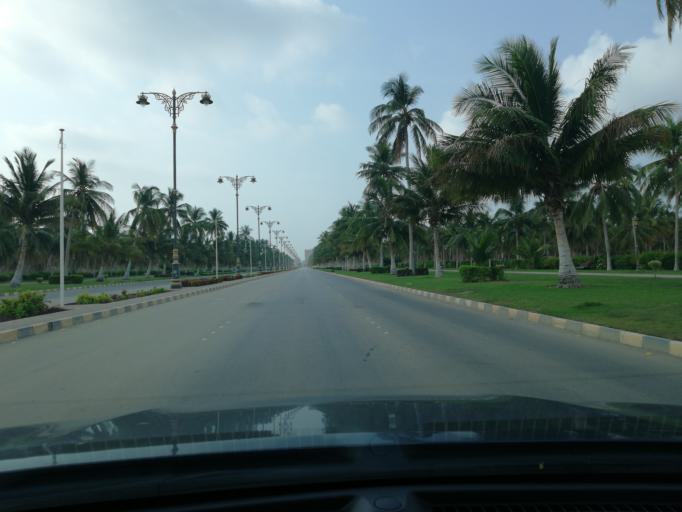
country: OM
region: Zufar
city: Salalah
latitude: 17.0347
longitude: 54.1080
